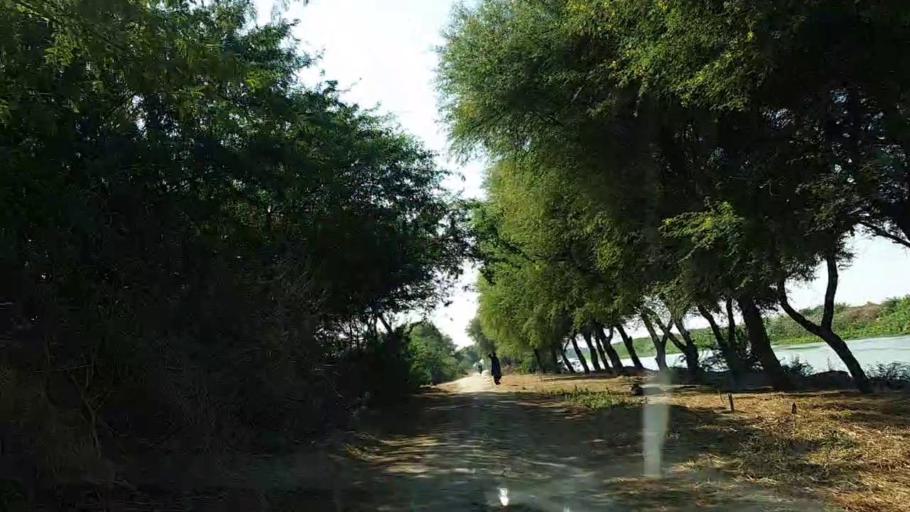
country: PK
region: Sindh
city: Chuhar Jamali
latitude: 24.5843
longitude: 68.0477
